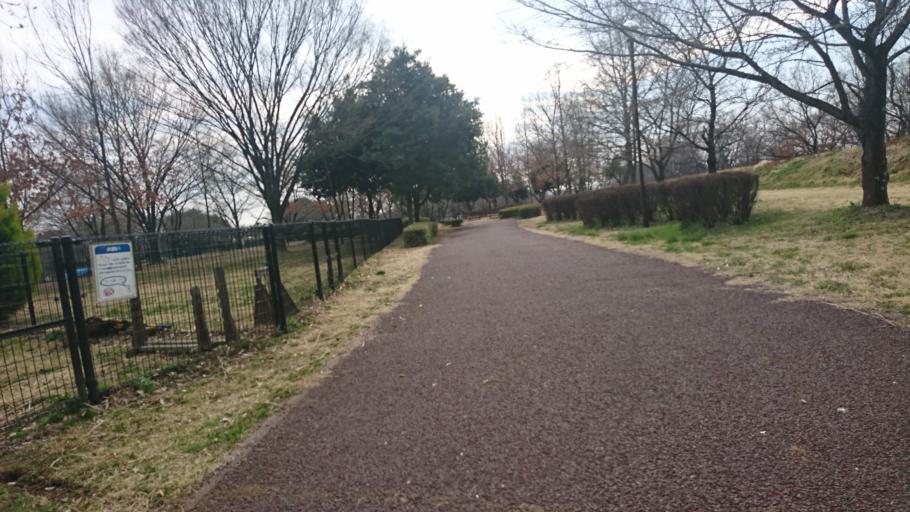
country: JP
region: Saitama
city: Kawagoe
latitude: 35.9153
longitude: 139.4508
